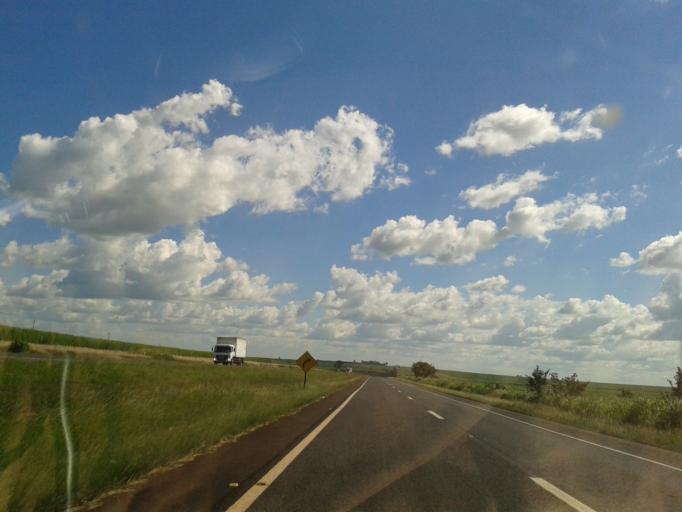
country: BR
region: Goias
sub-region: Morrinhos
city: Morrinhos
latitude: -17.8647
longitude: -49.2245
